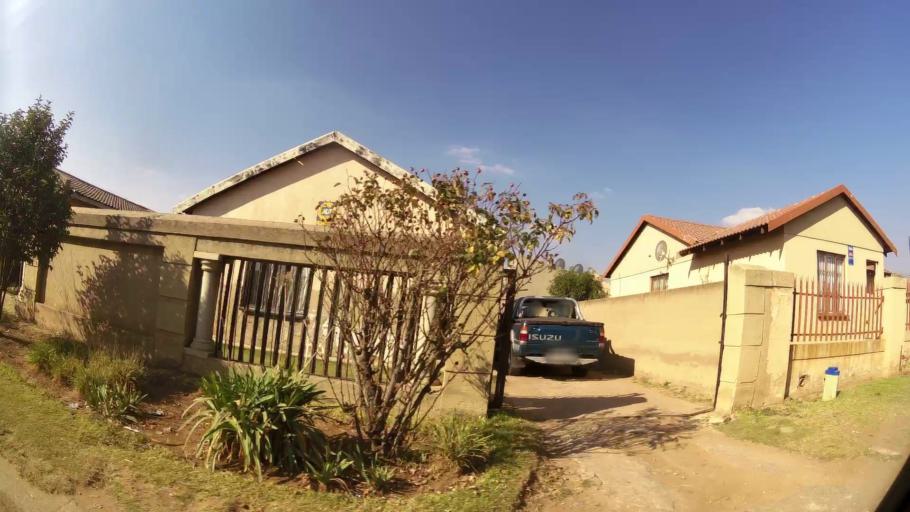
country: ZA
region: Gauteng
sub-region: Ekurhuleni Metropolitan Municipality
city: Benoni
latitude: -26.2255
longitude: 28.3251
